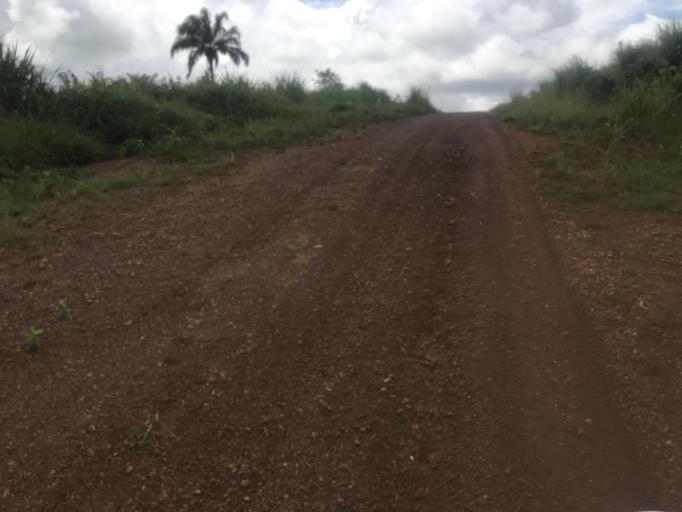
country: GN
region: Nzerekore
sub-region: Prefecture de Guekedou
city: Gueckedou
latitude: 8.4762
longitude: -10.2909
